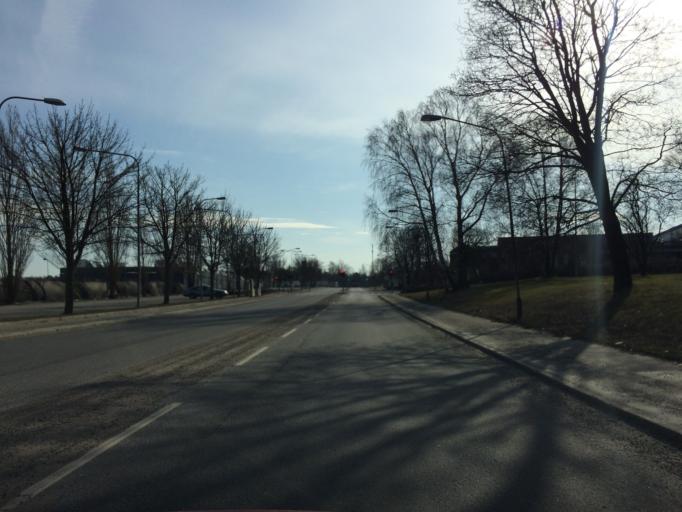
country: SE
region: Stockholm
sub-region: Stockholms Kommun
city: Arsta
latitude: 59.2927
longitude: 18.0159
